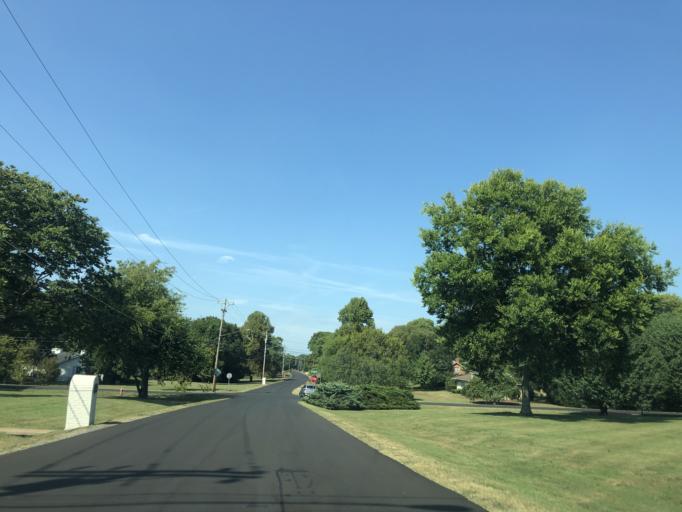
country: US
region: Tennessee
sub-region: Davidson County
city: Forest Hills
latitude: 36.0829
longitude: -86.8191
